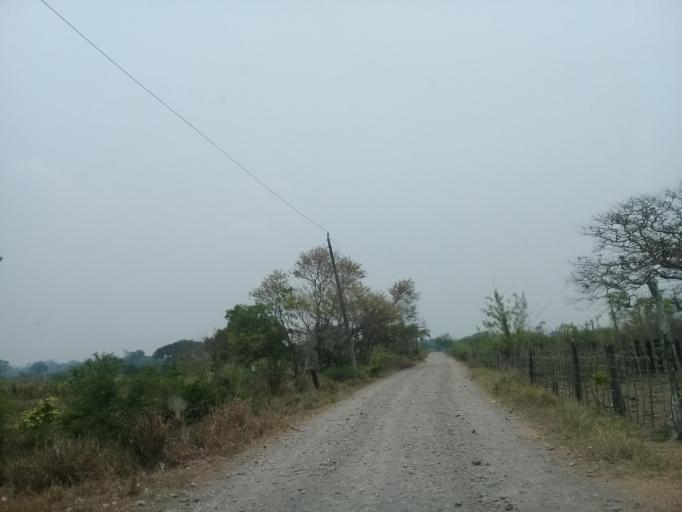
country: MX
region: Veracruz
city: Paso del Toro
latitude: 18.9798
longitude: -96.1727
